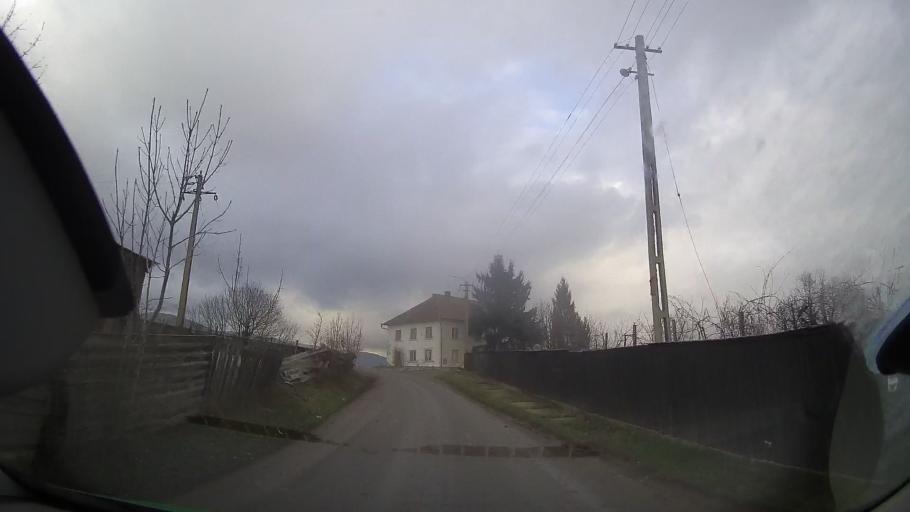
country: RO
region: Cluj
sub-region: Comuna Moldovenesti
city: Moldovenesti
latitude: 46.4995
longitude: 23.6765
